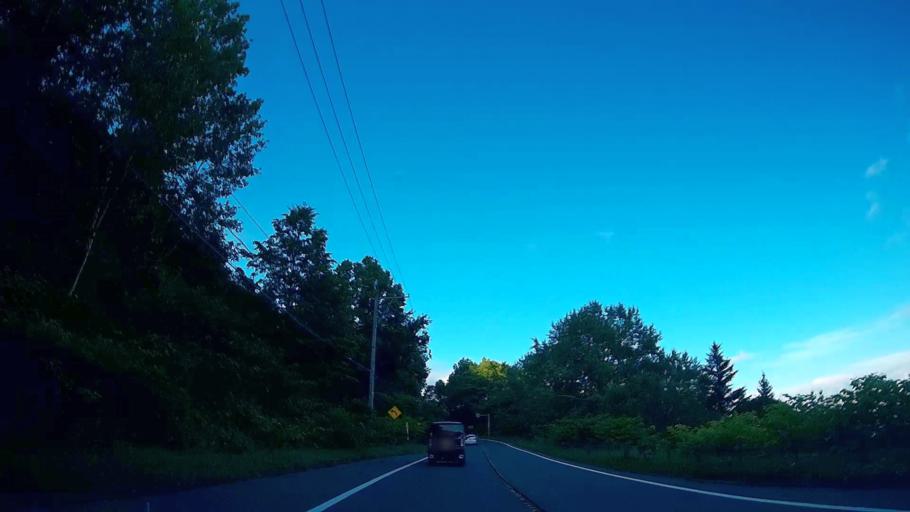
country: JP
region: Hokkaido
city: Date
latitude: 42.6083
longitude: 140.7752
